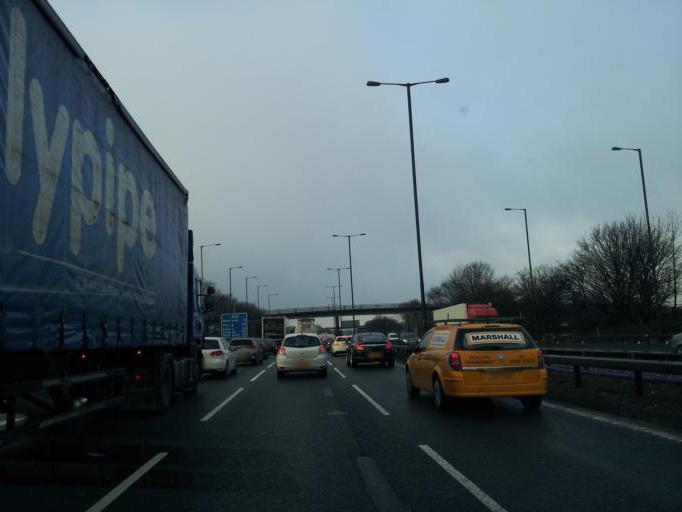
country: GB
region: England
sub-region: Manchester
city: Heywood
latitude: 53.5731
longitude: -2.2144
